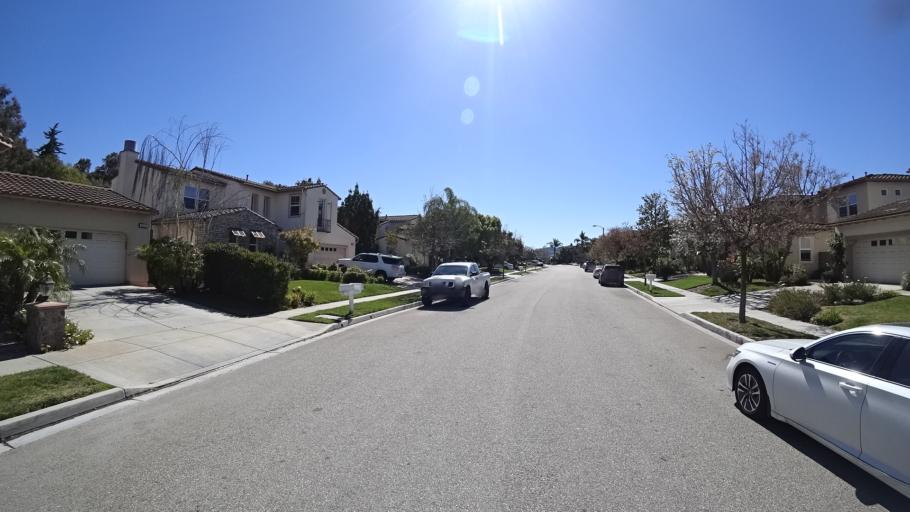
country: US
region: California
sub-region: Ventura County
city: Casa Conejo
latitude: 34.1777
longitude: -118.9823
